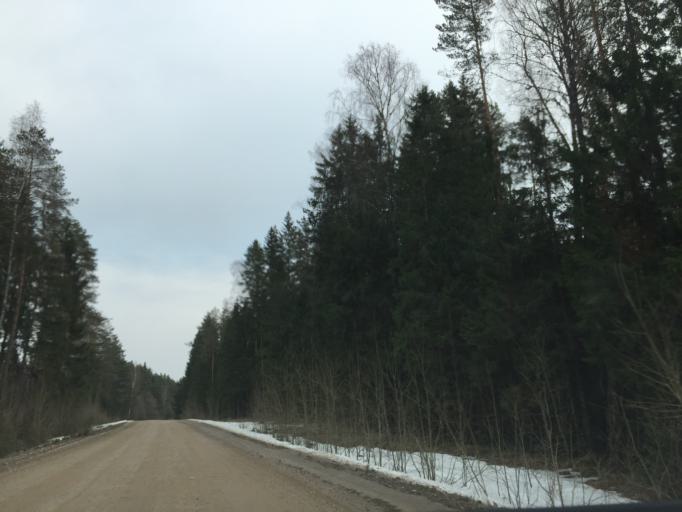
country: LV
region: Raunas
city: Rauna
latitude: 57.1641
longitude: 25.5129
